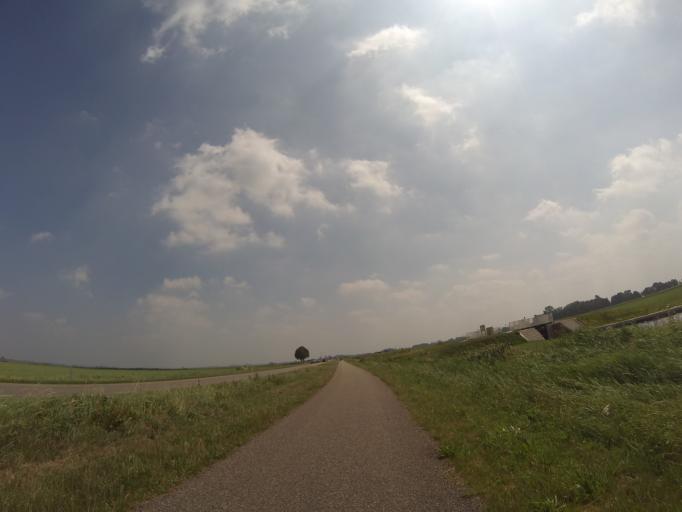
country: NL
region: Utrecht
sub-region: Gemeente Bunschoten
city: Bunschoten
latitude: 52.2303
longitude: 5.3930
